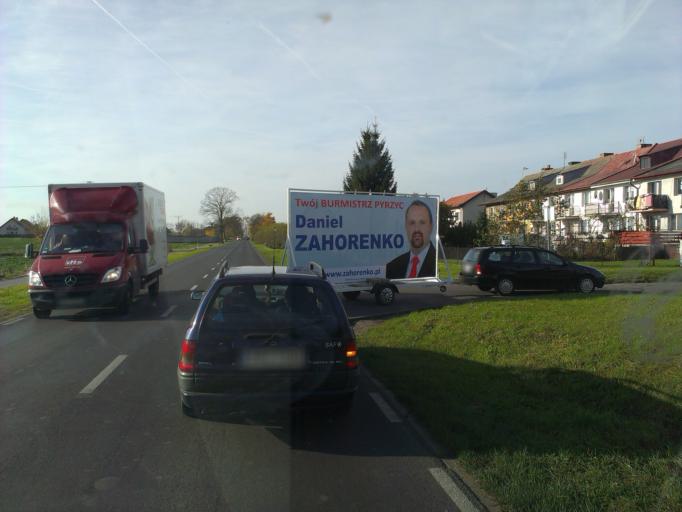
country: PL
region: West Pomeranian Voivodeship
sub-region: Powiat pyrzycki
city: Pyrzyce
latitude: 53.1367
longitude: 14.8828
